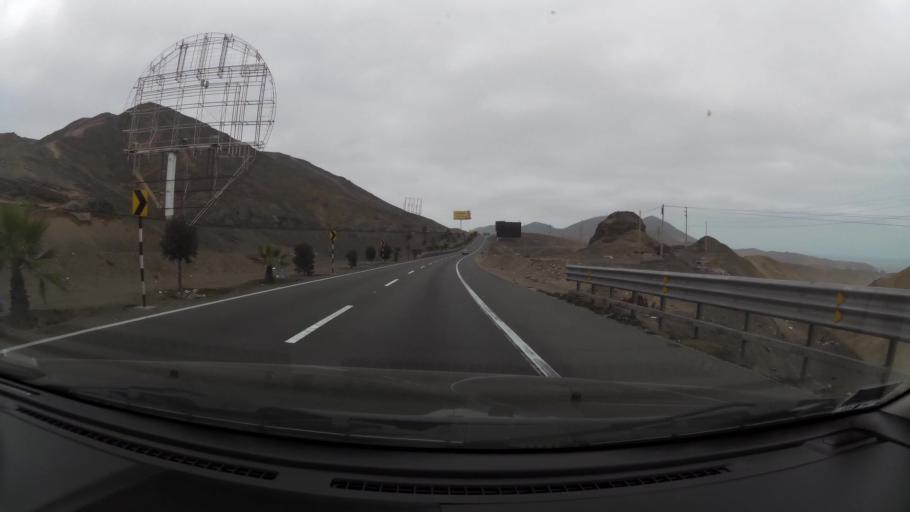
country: PE
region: Lima
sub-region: Lima
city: San Bartolo
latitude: -12.4306
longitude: -76.7536
